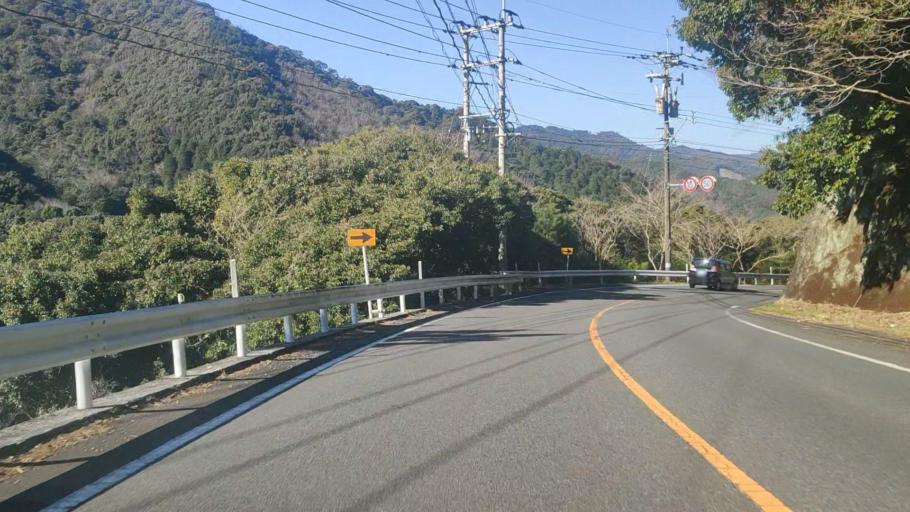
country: JP
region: Oita
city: Saiki
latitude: 32.8896
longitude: 131.9419
